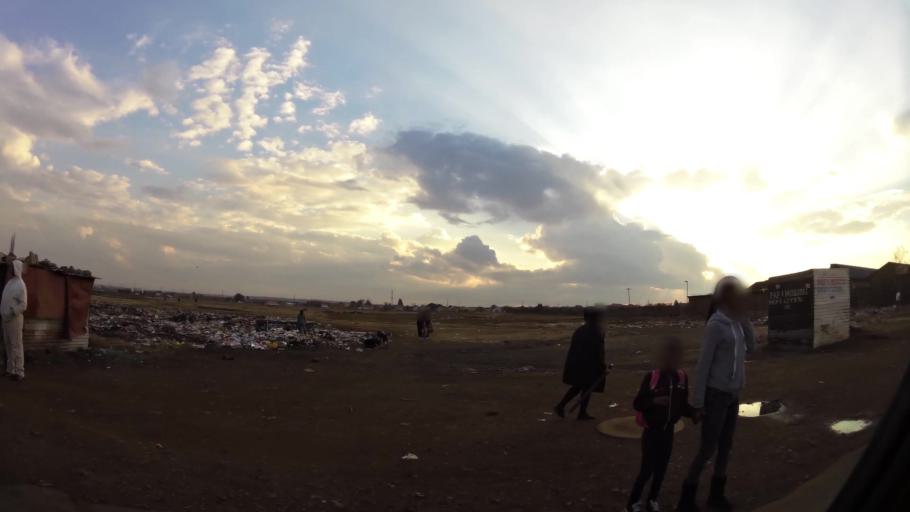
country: ZA
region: Gauteng
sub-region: City of Johannesburg Metropolitan Municipality
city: Orange Farm
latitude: -26.5392
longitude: 27.8324
